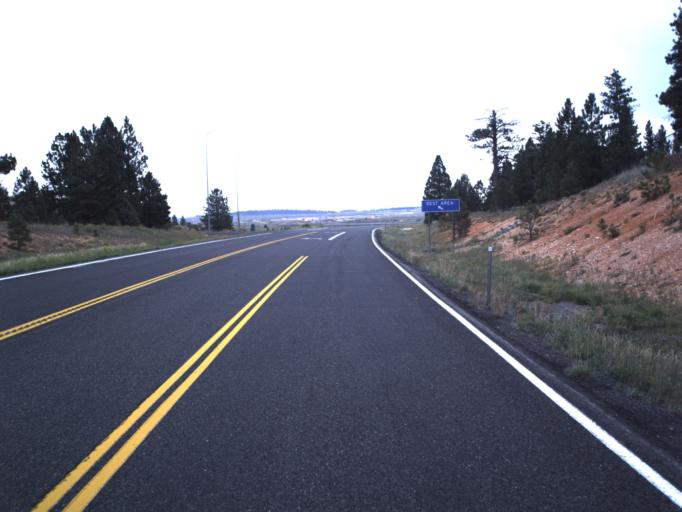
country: US
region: Utah
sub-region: Garfield County
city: Panguitch
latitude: 37.7082
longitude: -112.2069
